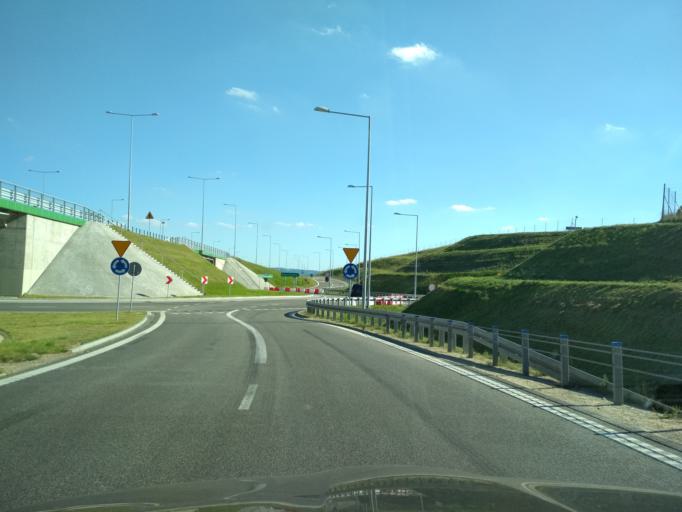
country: PL
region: Subcarpathian Voivodeship
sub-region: Powiat rzeszowski
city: Kielanowka
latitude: 50.0147
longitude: 21.9210
